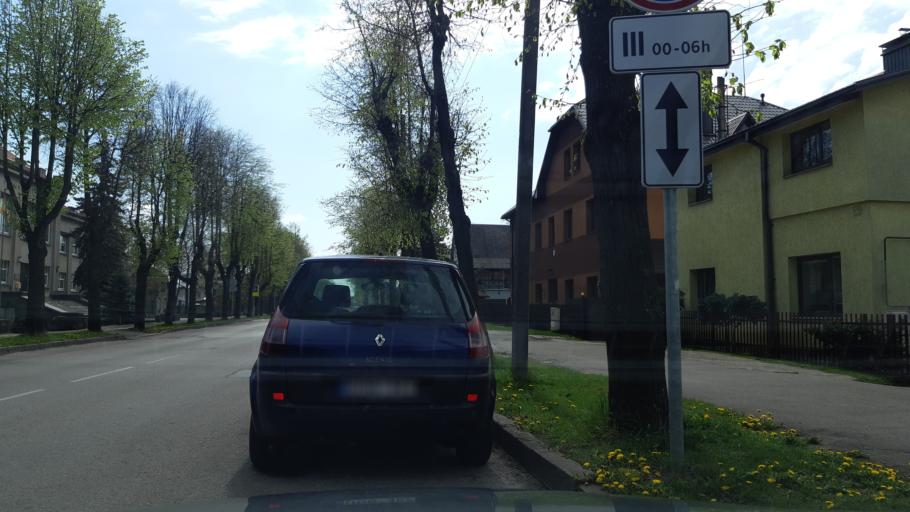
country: LT
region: Kauno apskritis
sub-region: Kaunas
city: Silainiai
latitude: 54.9087
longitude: 23.8784
